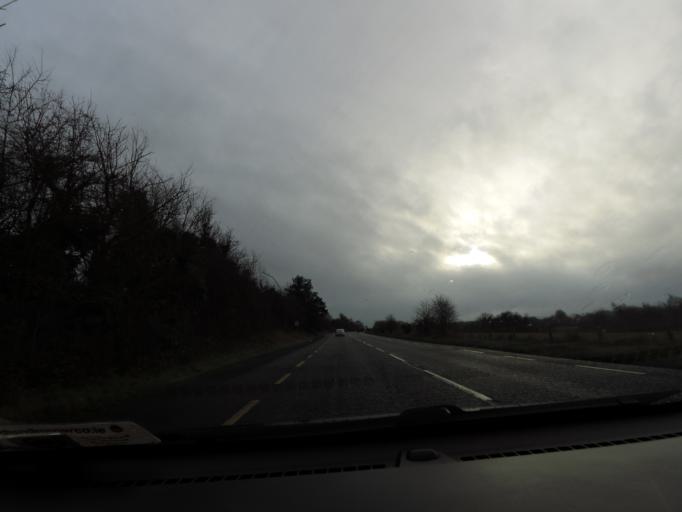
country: IE
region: Munster
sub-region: North Tipperary
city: Roscrea
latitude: 52.9920
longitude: -7.8635
